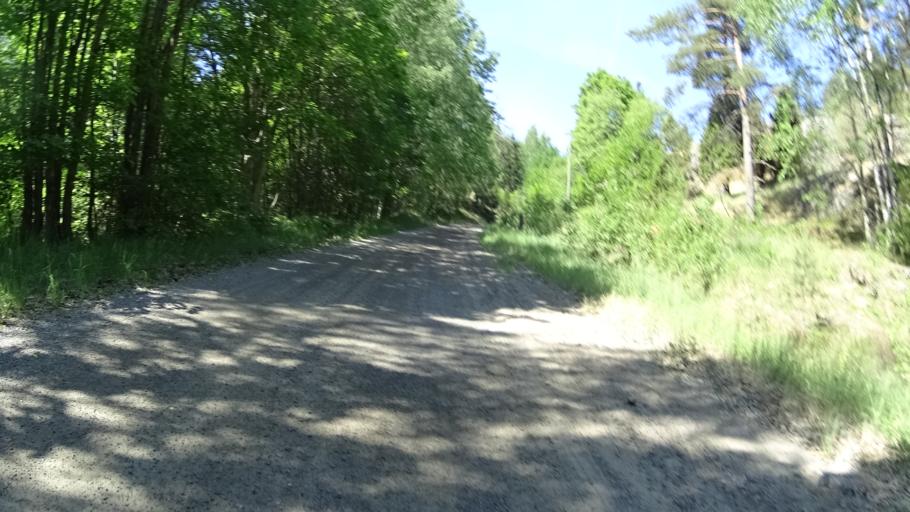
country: FI
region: Uusimaa
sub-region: Raaseporin
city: Pohja
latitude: 60.0948
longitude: 23.5657
